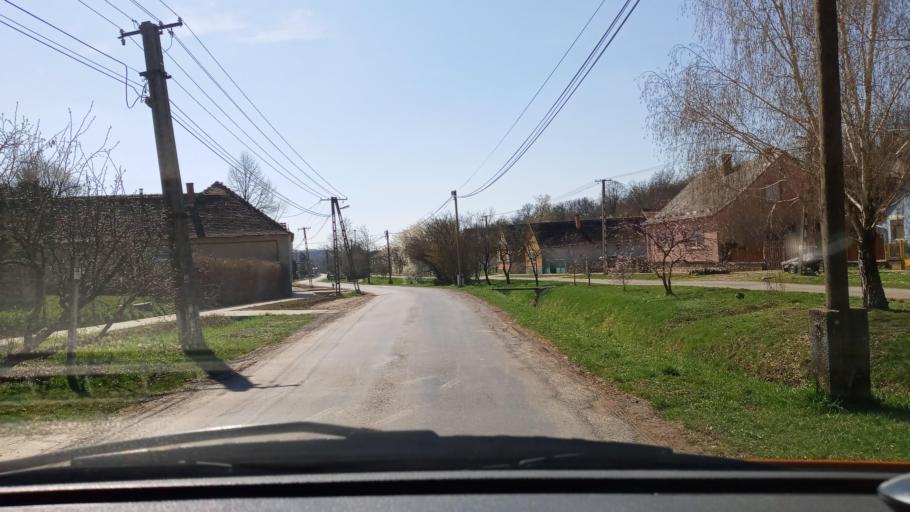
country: HU
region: Baranya
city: Pecsvarad
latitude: 46.0648
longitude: 18.4495
